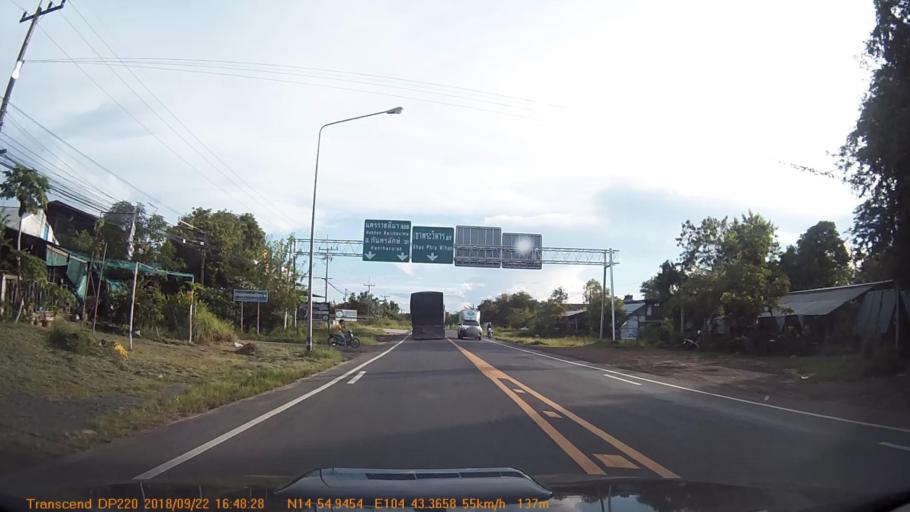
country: TH
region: Sisaket
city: Non Kho
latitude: 14.9158
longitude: 104.7228
